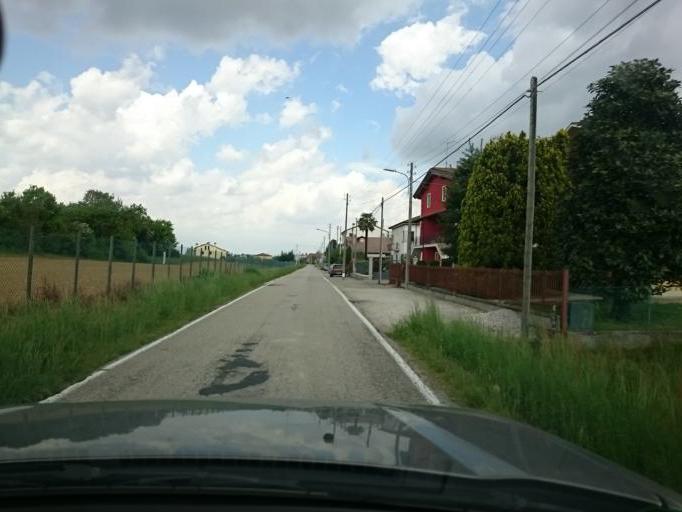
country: IT
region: Veneto
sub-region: Provincia di Vicenza
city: Longare
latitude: 45.5063
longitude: 11.5846
